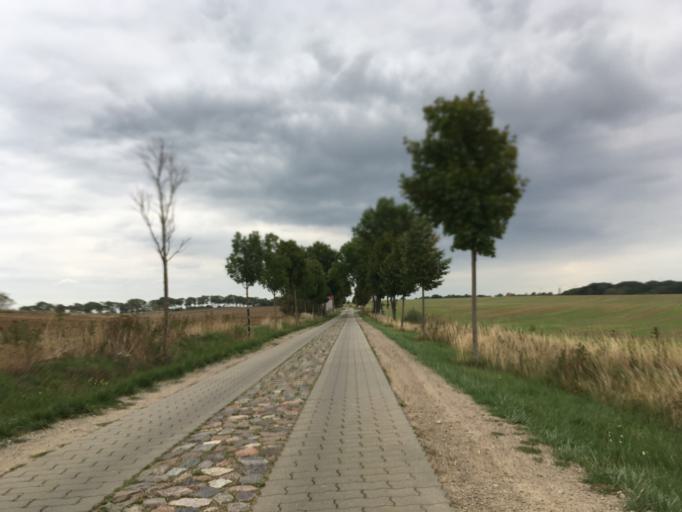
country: DE
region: Brandenburg
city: Pinnow
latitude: 53.0840
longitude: 14.1129
